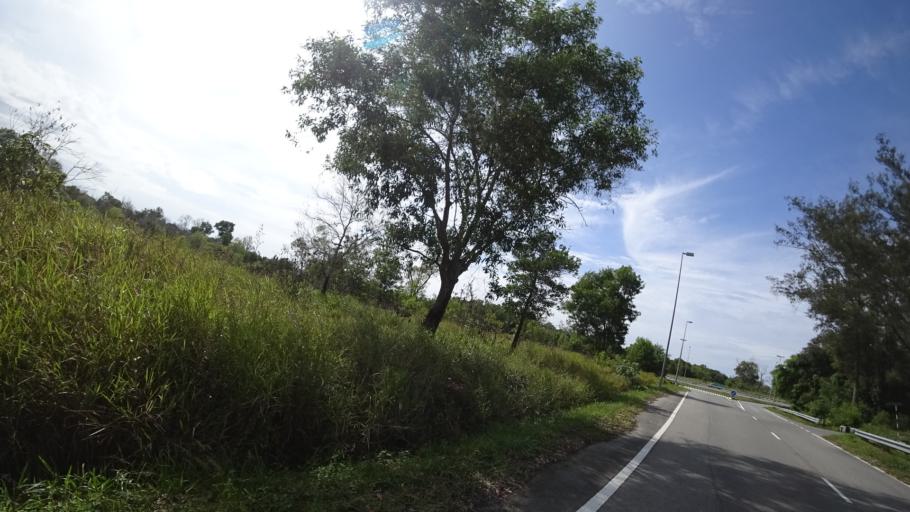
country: BN
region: Tutong
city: Tutong
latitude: 4.8221
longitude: 114.6620
